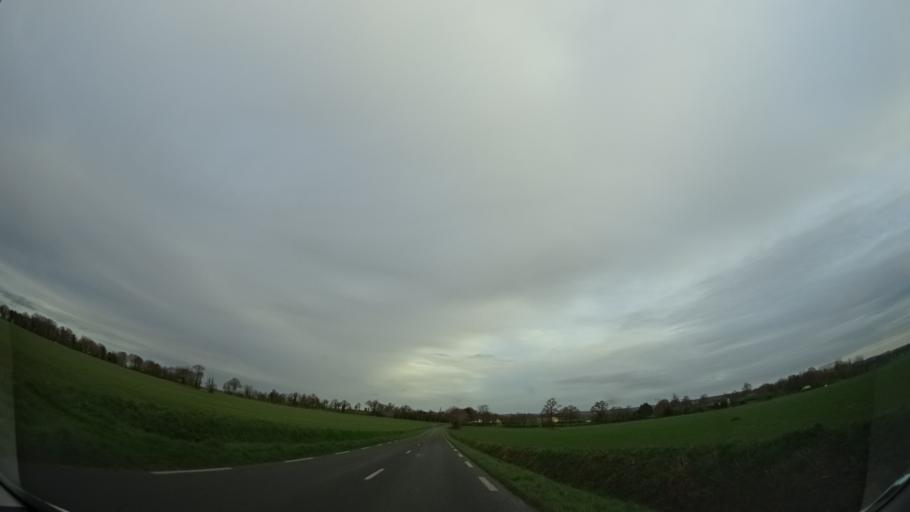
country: FR
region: Brittany
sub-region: Departement des Cotes-d'Armor
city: Evran
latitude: 48.3590
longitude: -1.9694
